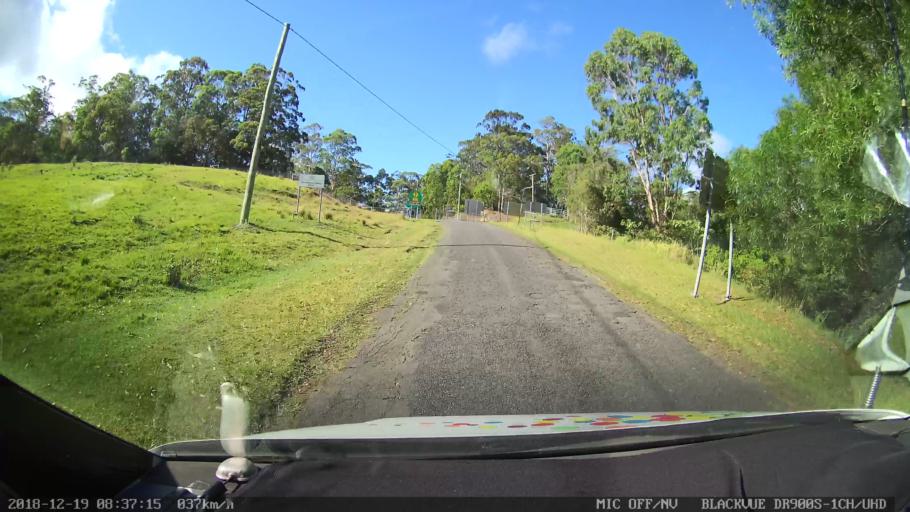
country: AU
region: New South Wales
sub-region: Kyogle
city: Kyogle
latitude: -28.3311
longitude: 152.9732
